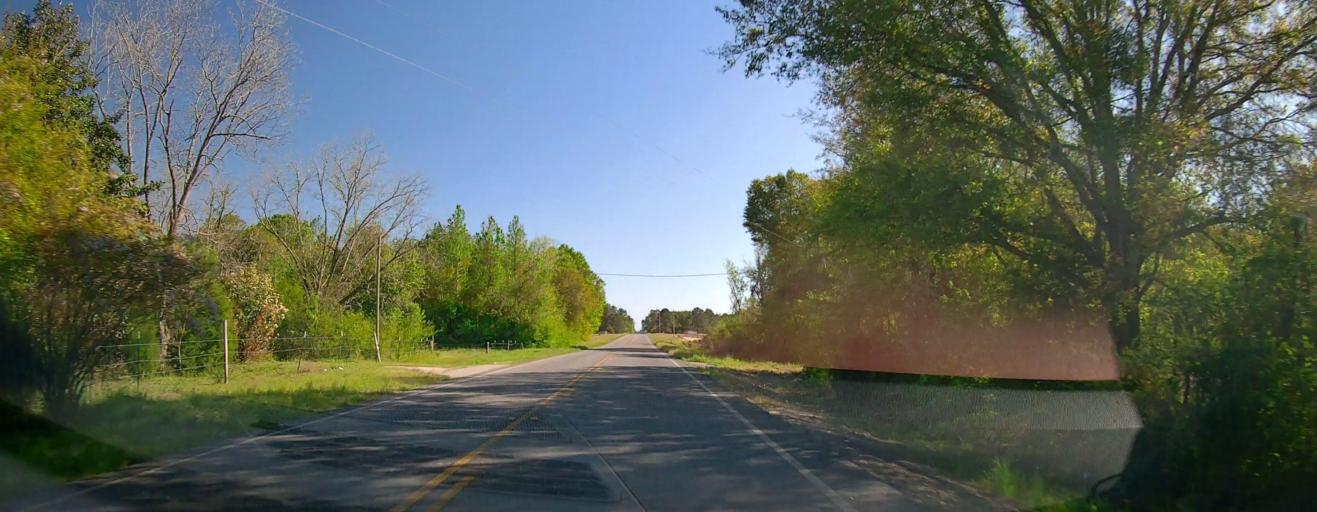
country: US
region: Georgia
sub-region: Wilcox County
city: Rochelle
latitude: 32.0911
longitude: -83.5033
